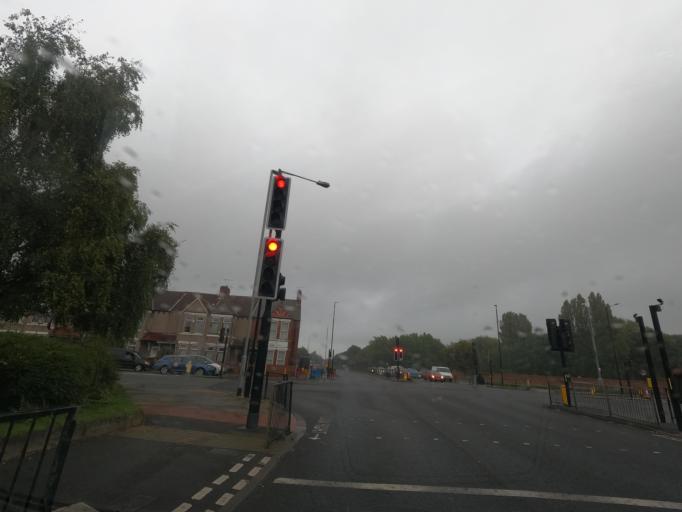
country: GB
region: England
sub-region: Middlesbrough
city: Middlesbrough
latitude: 54.5669
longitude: -1.2099
